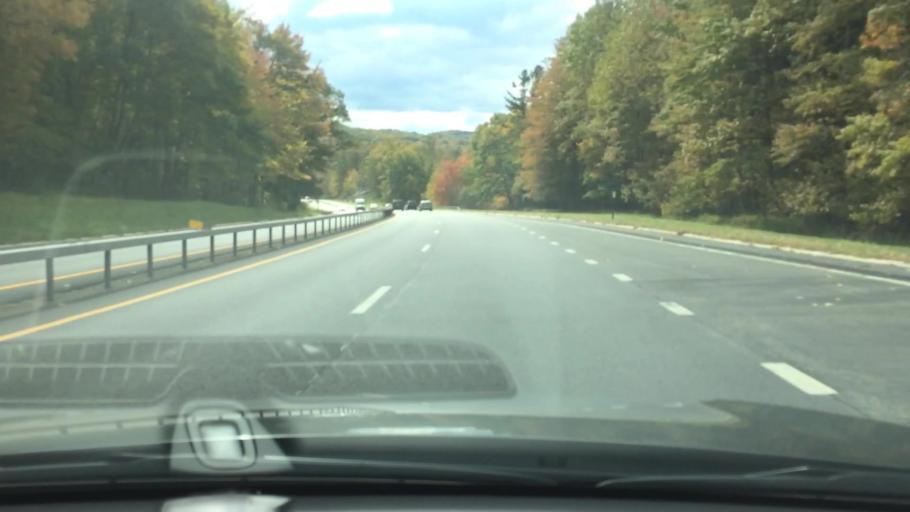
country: US
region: New York
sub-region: Dutchess County
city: Brinckerhoff
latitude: 41.5072
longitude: -73.7947
